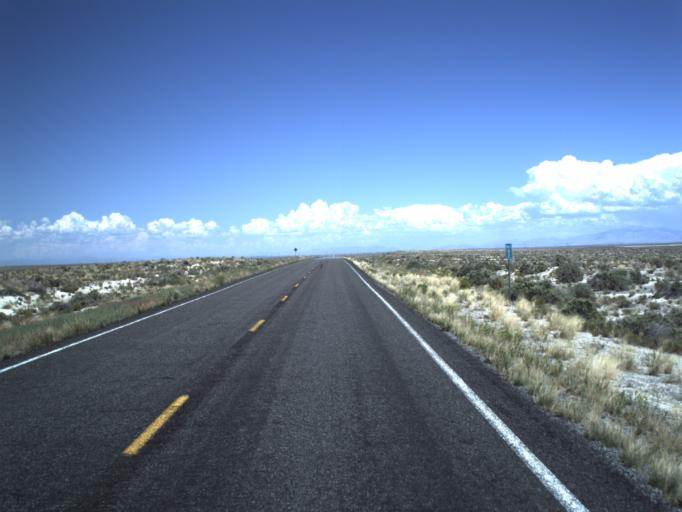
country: US
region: Utah
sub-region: Millard County
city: Delta
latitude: 39.1882
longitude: -113.0041
